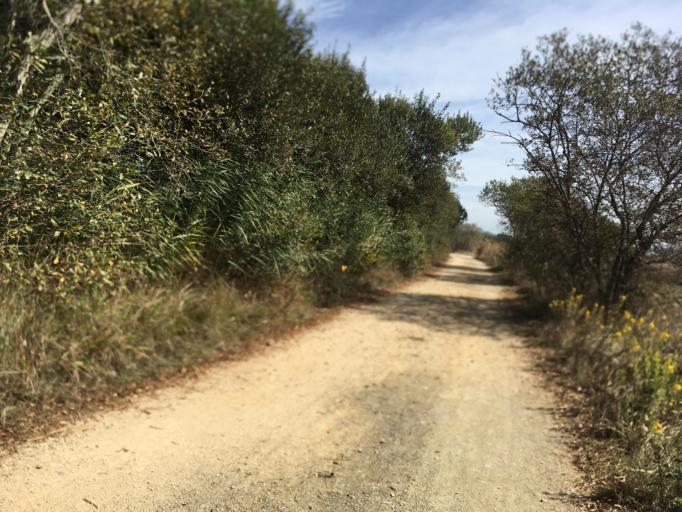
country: PT
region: Aveiro
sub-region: Estarreja
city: Salreu
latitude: 40.7322
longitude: -8.5769
